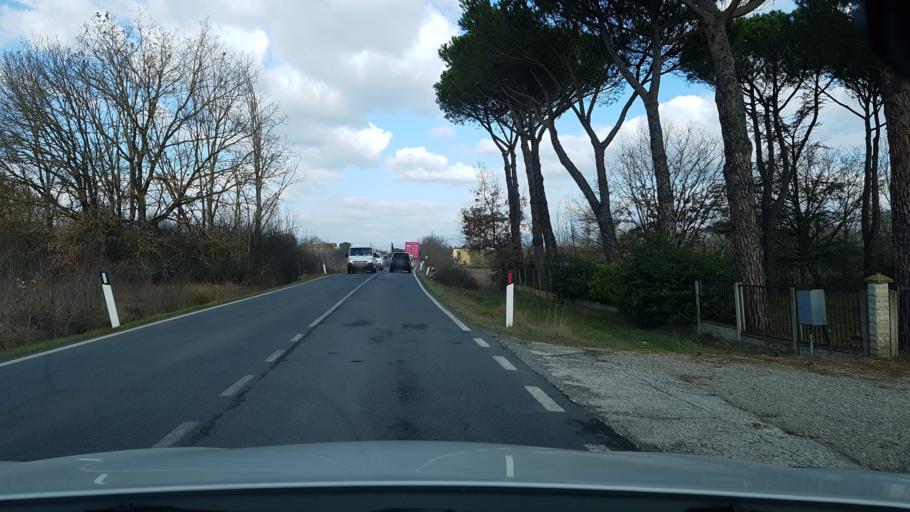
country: IT
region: Umbria
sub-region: Provincia di Perugia
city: Castiglione del Lago
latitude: 43.1617
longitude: 12.0160
